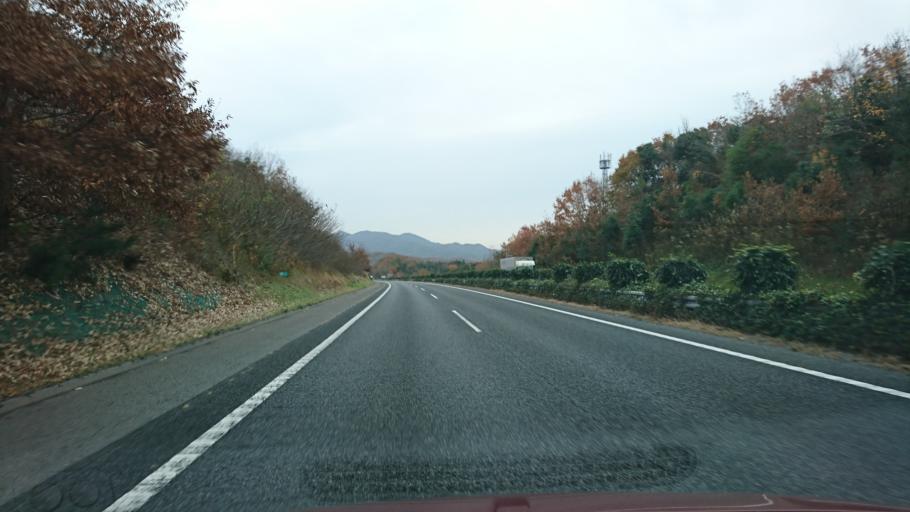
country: JP
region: Hyogo
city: Miki
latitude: 34.8034
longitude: 135.0350
